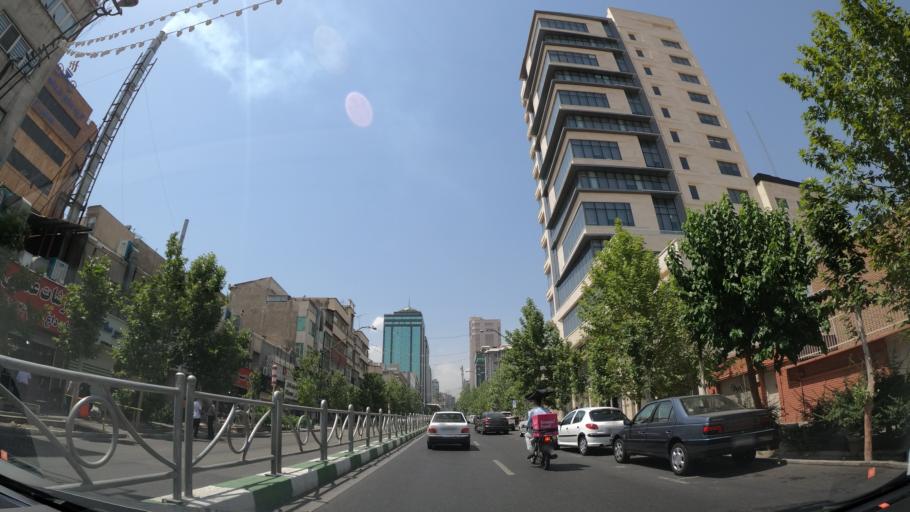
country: IR
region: Tehran
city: Tehran
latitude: 35.7299
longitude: 51.4123
